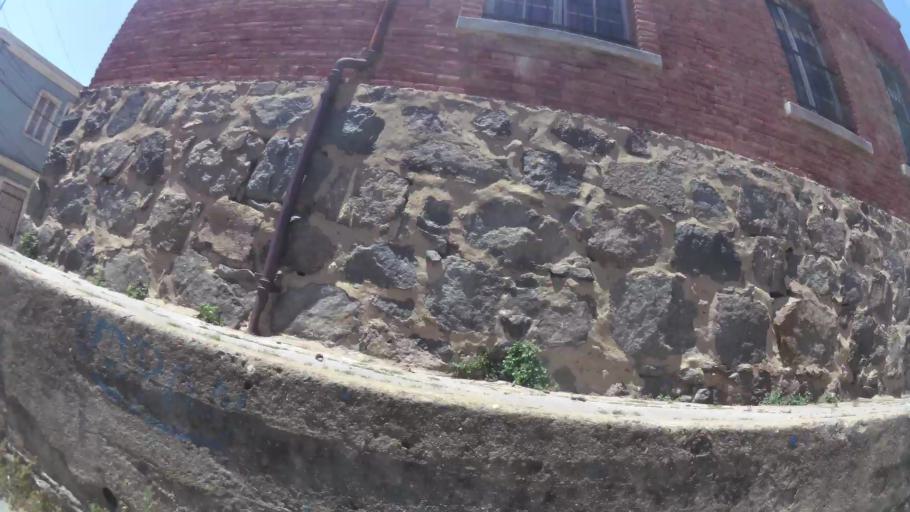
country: CL
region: Valparaiso
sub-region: Provincia de Valparaiso
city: Valparaiso
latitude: -33.0413
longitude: -71.6351
